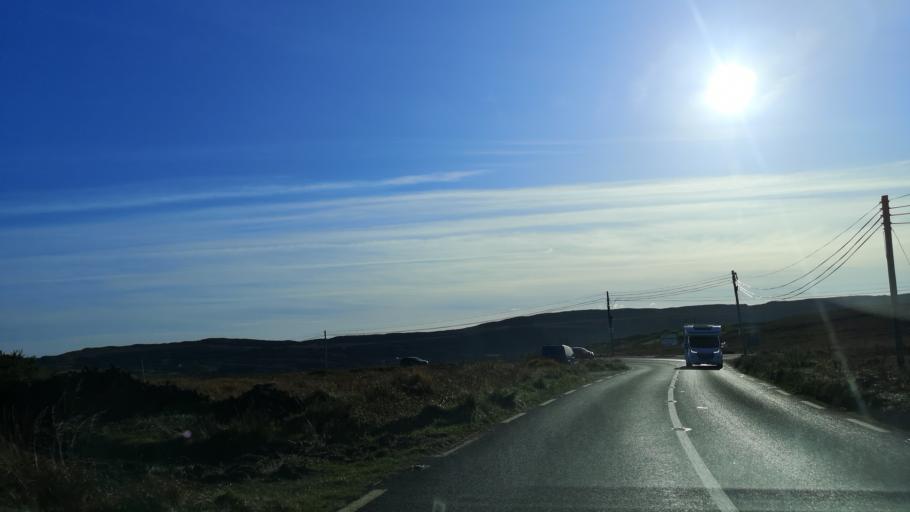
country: IE
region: Connaught
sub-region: County Galway
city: Clifden
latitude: 53.5240
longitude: -10.0479
